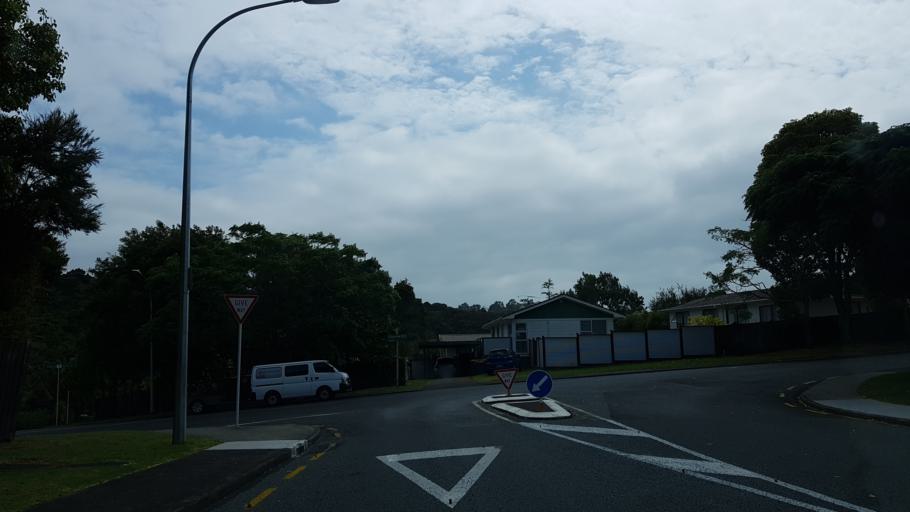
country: NZ
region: Auckland
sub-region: Auckland
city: North Shore
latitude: -36.7715
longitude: 174.7049
